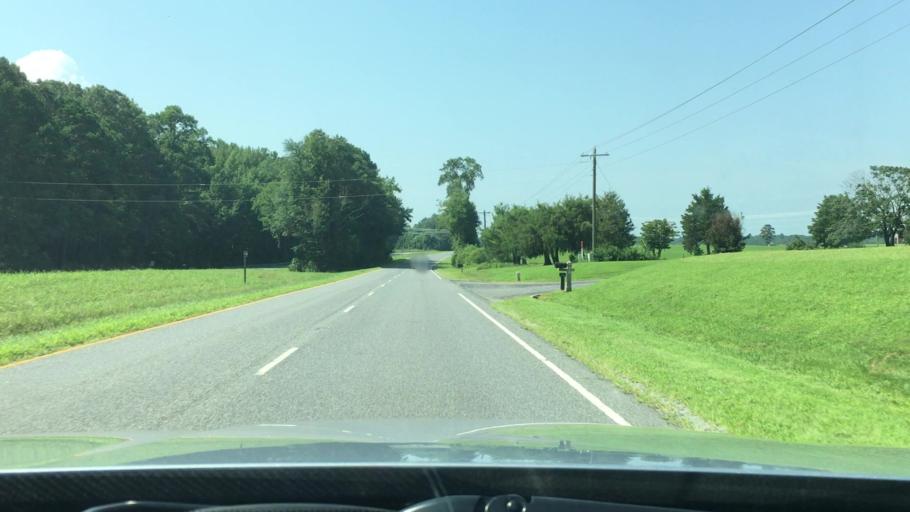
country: US
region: Virginia
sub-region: Caroline County
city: Bowling Green
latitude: 37.9808
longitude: -77.4215
